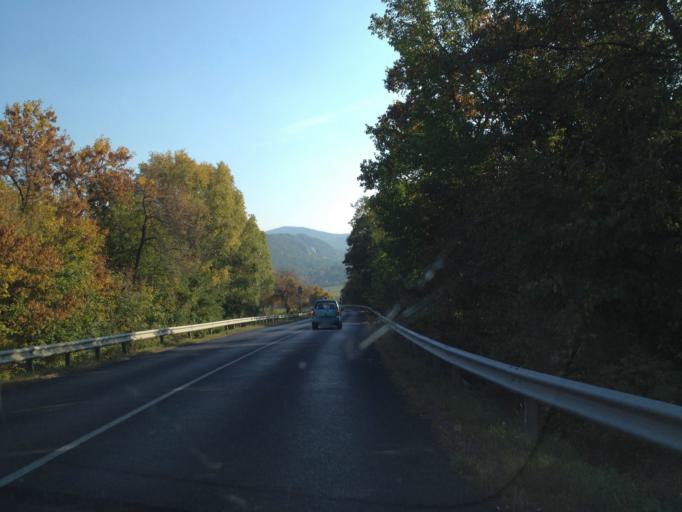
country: HU
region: Pest
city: Csobanka
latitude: 47.6668
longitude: 18.9649
